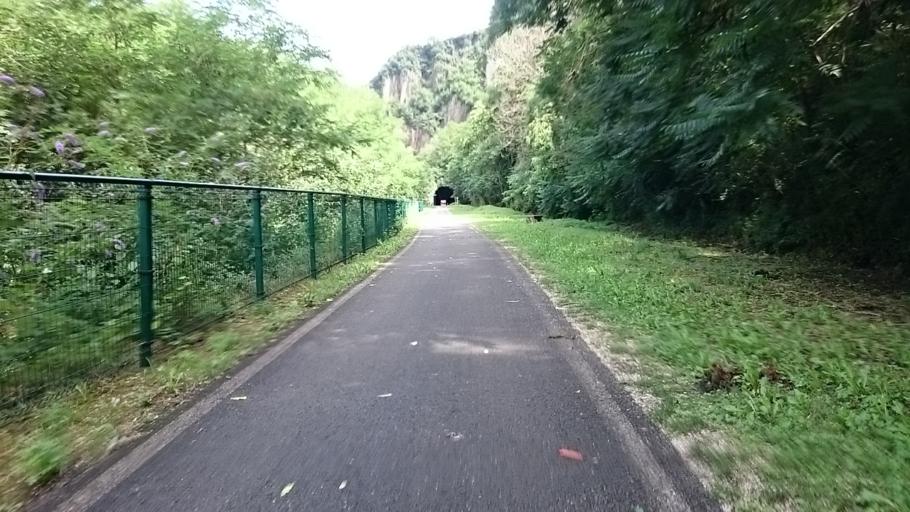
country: IT
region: Trentino-Alto Adige
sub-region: Bolzano
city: Fie Allo Sciliar
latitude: 46.5231
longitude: 11.4880
